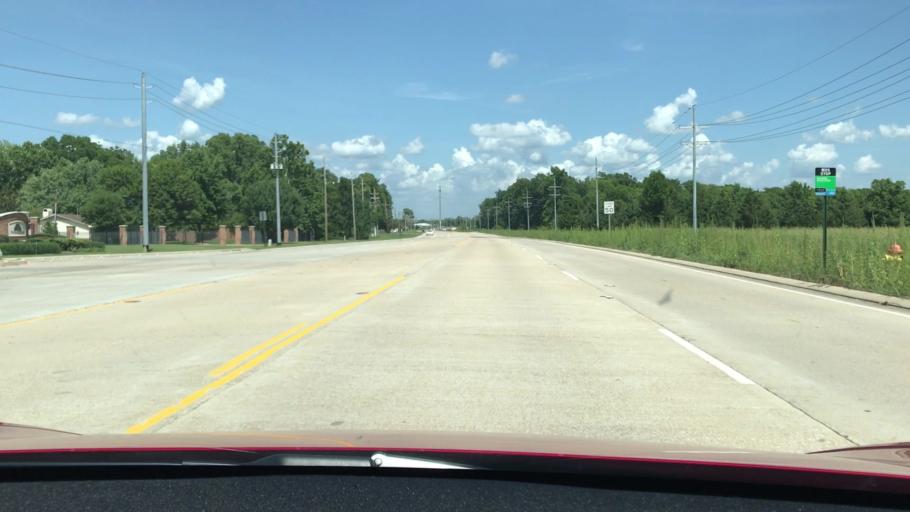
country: US
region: Louisiana
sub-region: Bossier Parish
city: Bossier City
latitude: 32.4009
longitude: -93.7038
